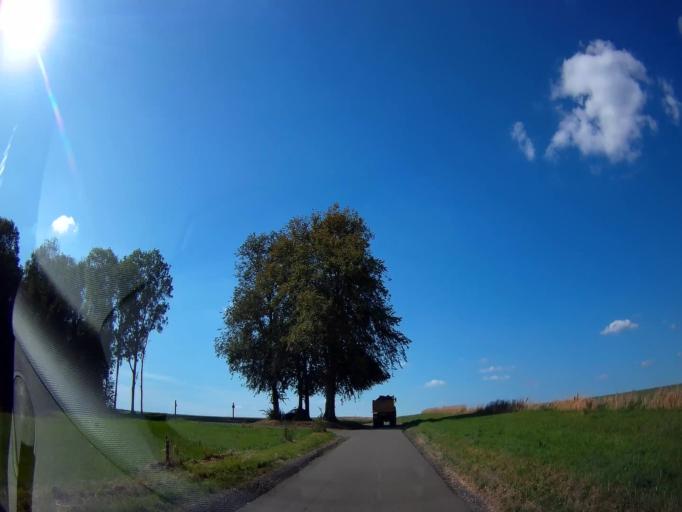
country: BE
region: Wallonia
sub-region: Province de Namur
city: Dinant
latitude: 50.2361
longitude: 4.9692
